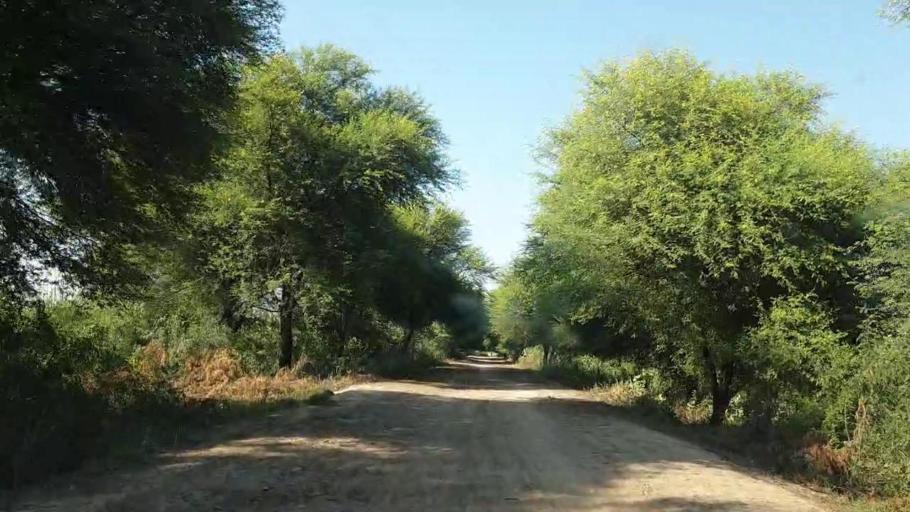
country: PK
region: Sindh
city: Tando Jam
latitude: 25.3605
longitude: 68.5696
